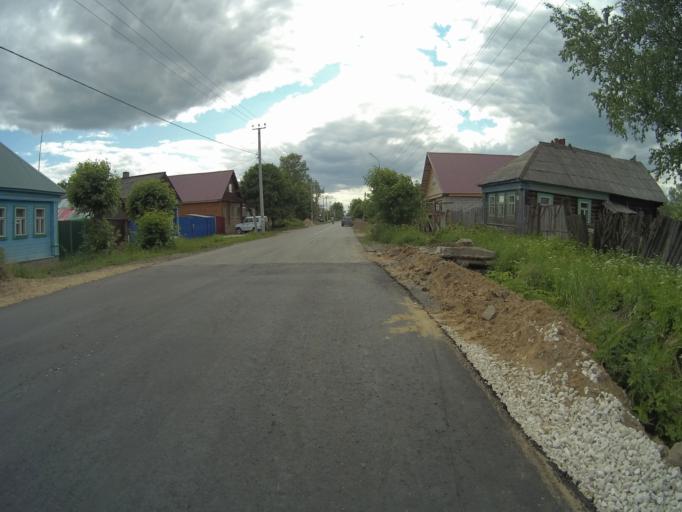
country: RU
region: Vladimir
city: Sudogda
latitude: 55.9531
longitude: 40.8572
